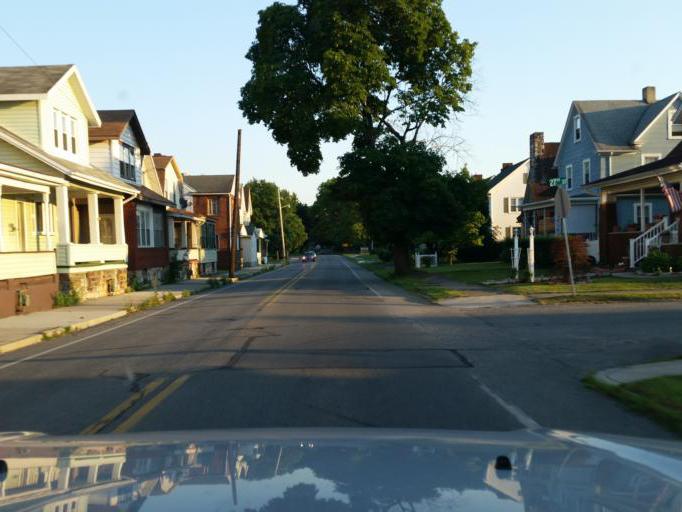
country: US
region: Pennsylvania
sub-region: Blair County
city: Altoona
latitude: 40.4989
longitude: -78.4061
